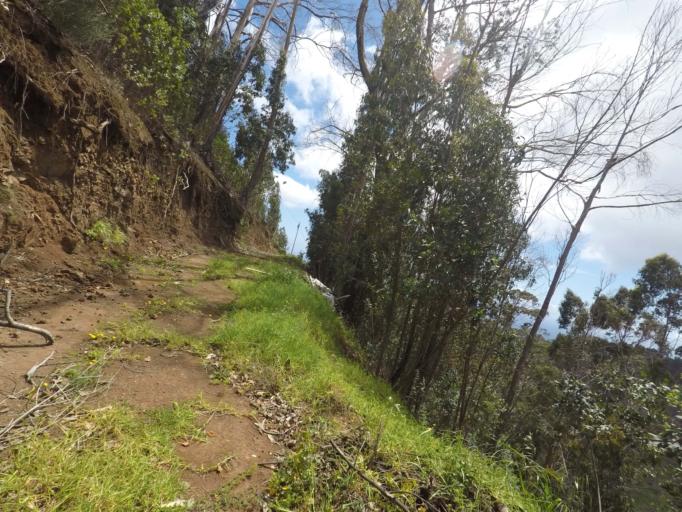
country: PT
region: Madeira
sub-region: Calheta
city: Estreito da Calheta
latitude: 32.7457
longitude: -17.1951
